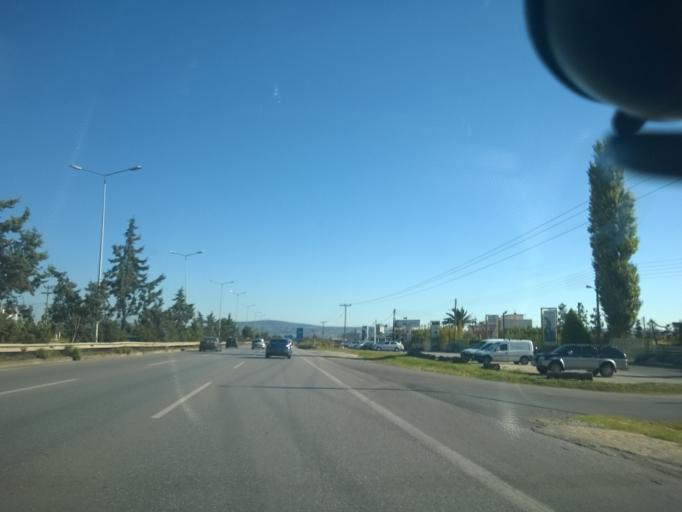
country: GR
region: Central Macedonia
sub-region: Nomos Thessalonikis
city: Thermi
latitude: 40.5485
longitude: 23.0026
